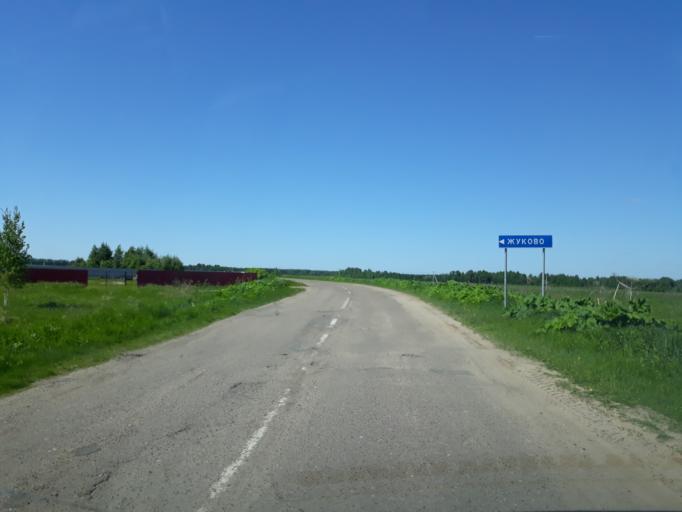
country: RU
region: Jaroslavl
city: Yaroslavl
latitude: 57.6788
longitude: 40.0185
